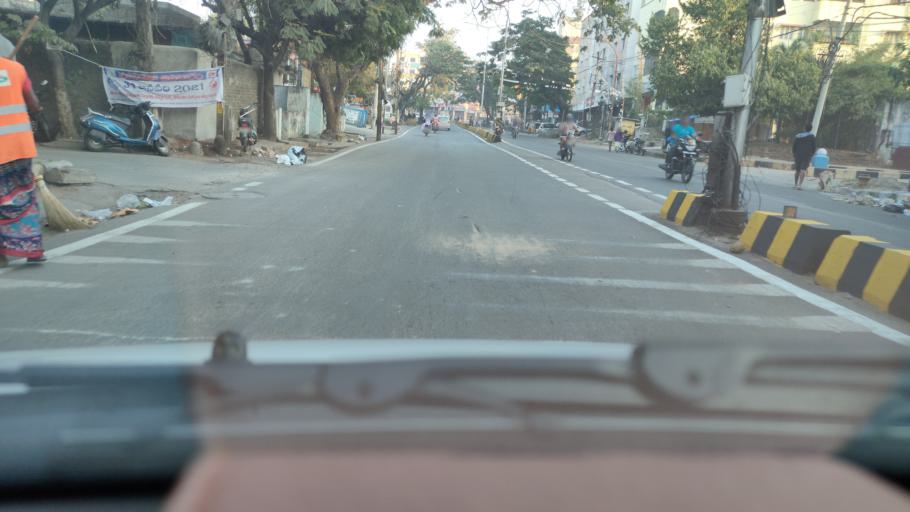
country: IN
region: Telangana
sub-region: Rangareddi
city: Gaddi Annaram
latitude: 17.3904
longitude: 78.5163
